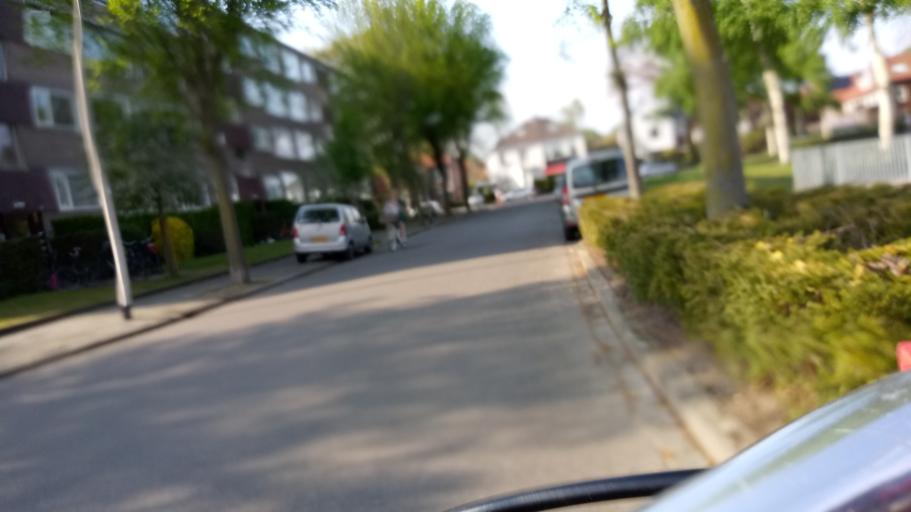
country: NL
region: Gelderland
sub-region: Gemeente Nijmegen
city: Nijmegen
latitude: 51.8268
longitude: 5.8515
